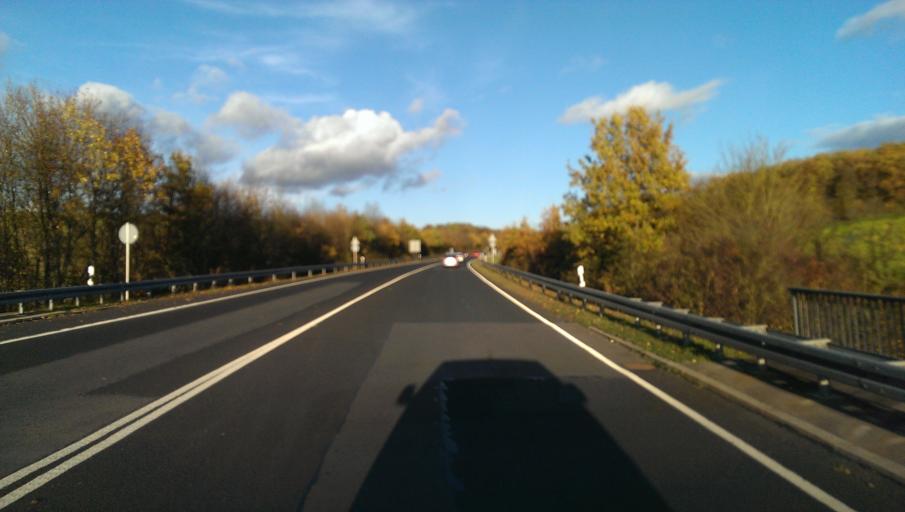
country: DE
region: Bavaria
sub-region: Regierungsbezirk Unterfranken
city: Arnstein
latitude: 49.9950
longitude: 9.9850
